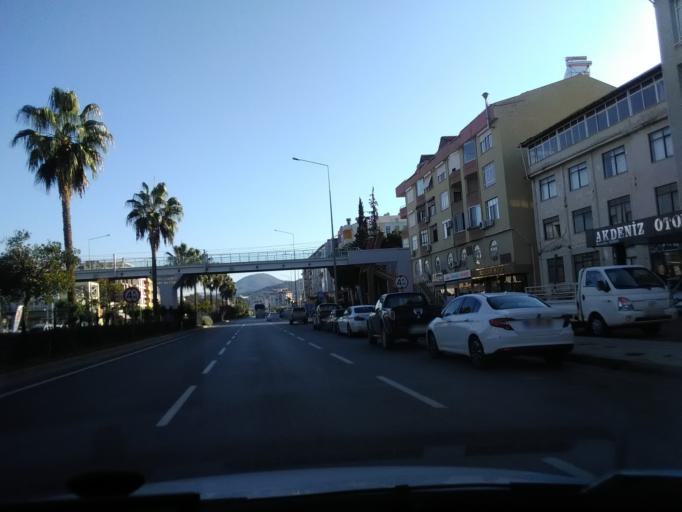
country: TR
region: Antalya
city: Gazipasa
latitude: 36.2705
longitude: 32.3124
